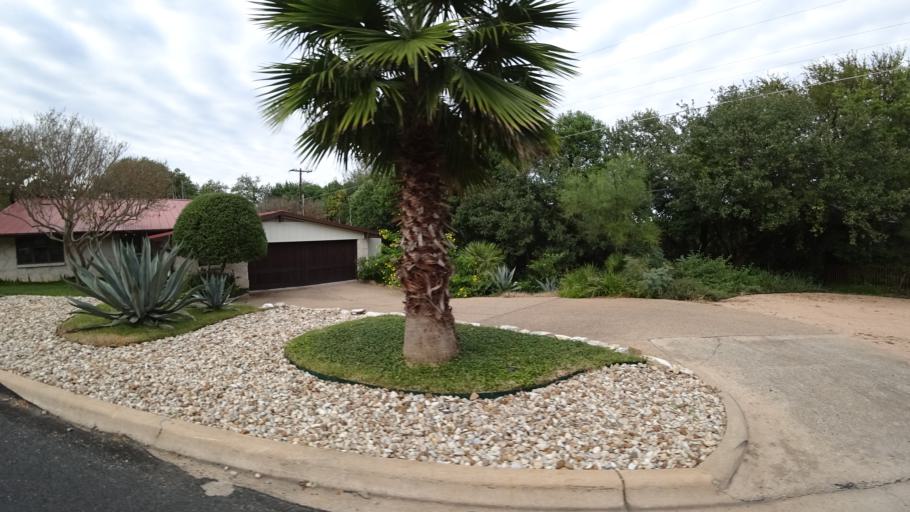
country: US
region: Texas
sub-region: Travis County
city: Rollingwood
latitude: 30.2831
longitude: -97.7873
